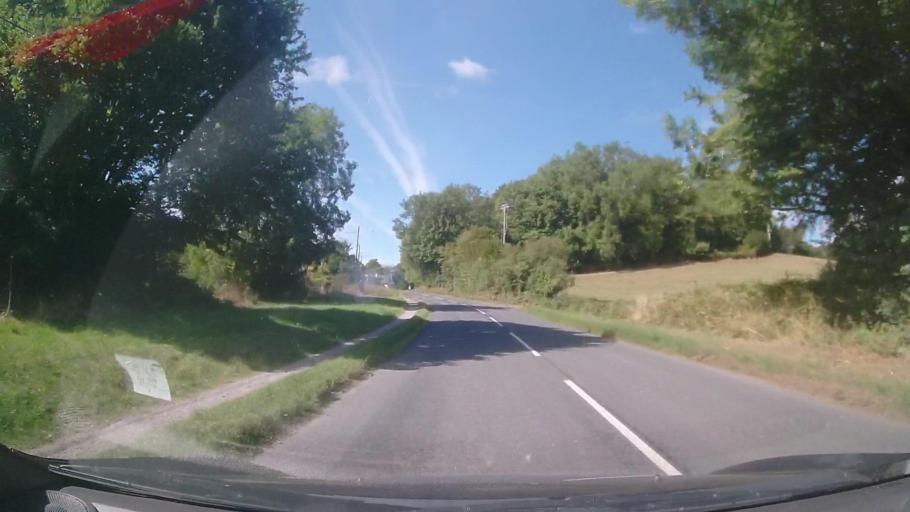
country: GB
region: Wales
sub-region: Sir Powys
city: Hay
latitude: 52.0838
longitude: -3.1459
